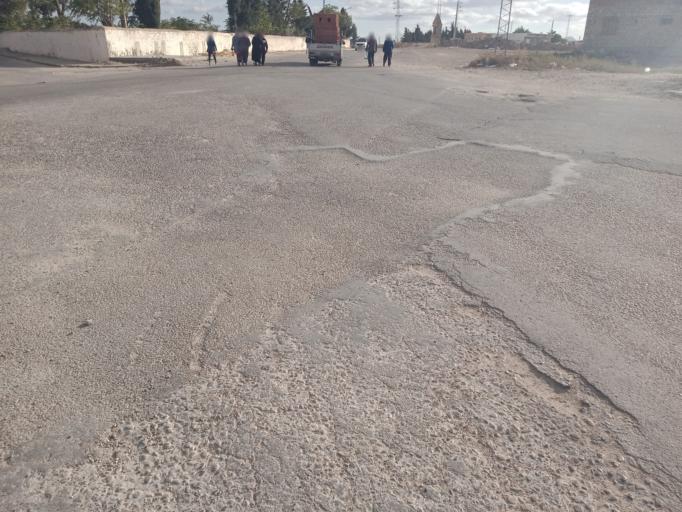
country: TN
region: Silyanah
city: Maktar
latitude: 35.8537
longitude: 9.2038
